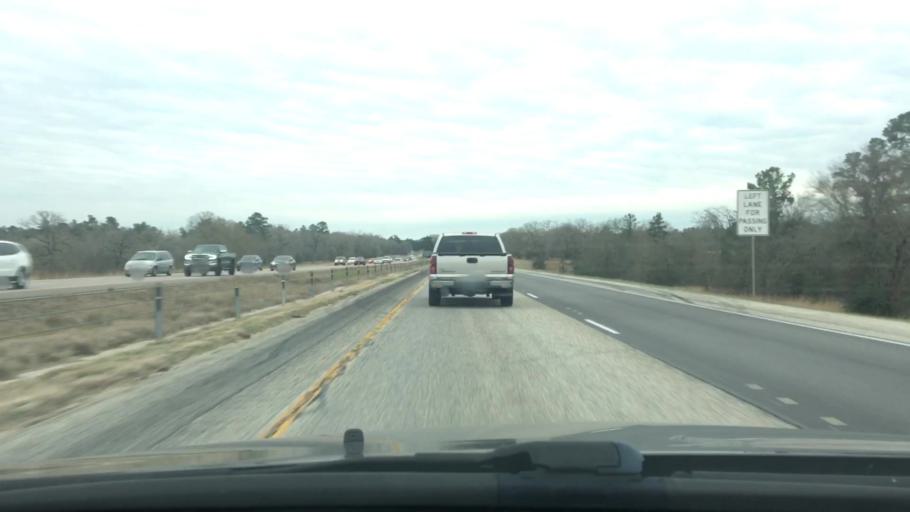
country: US
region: Texas
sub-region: Walker County
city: Huntsville
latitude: 30.7709
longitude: -95.6417
